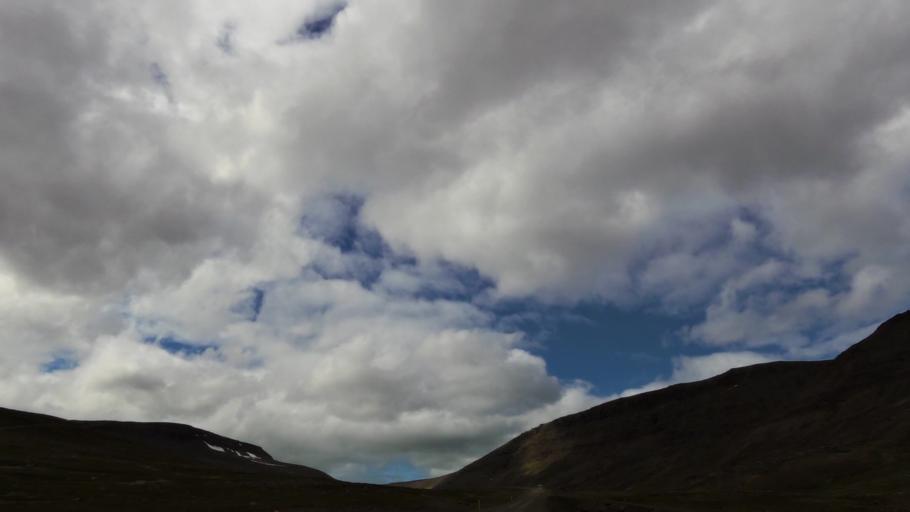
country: IS
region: Westfjords
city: Isafjoerdur
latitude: 66.1599
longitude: -23.2987
